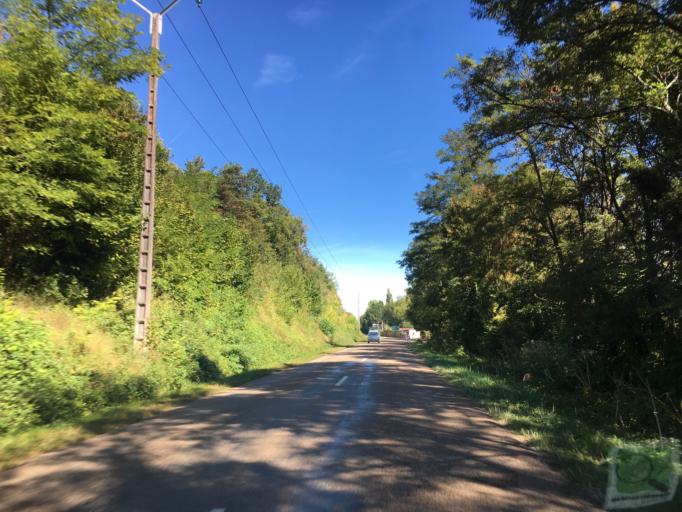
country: FR
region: Bourgogne
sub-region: Departement de l'Yonne
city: Vermenton
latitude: 47.6391
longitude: 3.6575
